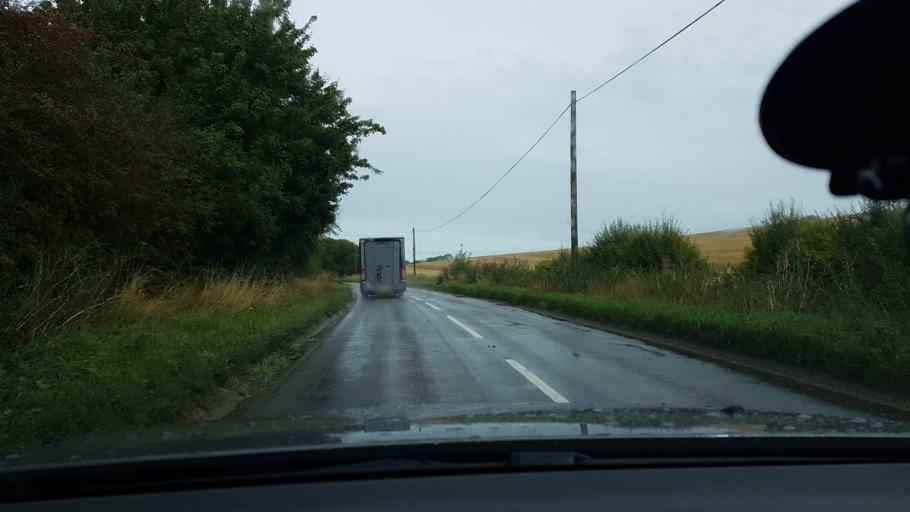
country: GB
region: England
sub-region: West Berkshire
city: Lambourn
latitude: 51.5155
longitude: -1.5231
